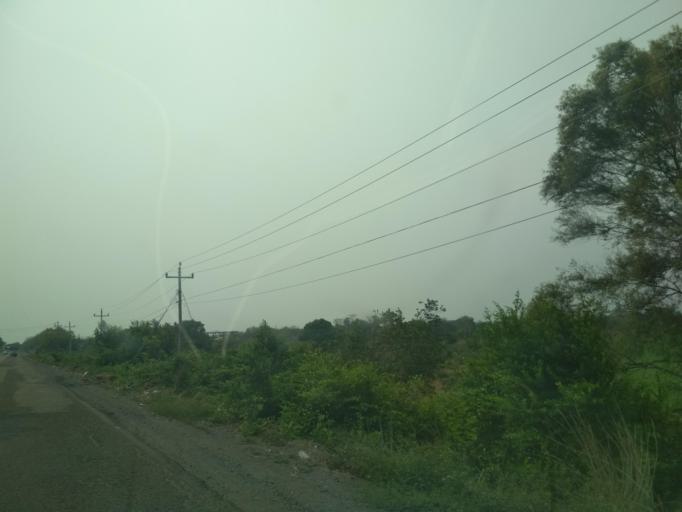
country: MX
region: Veracruz
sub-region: Veracruz
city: Delfino Victoria (Santa Fe)
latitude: 19.2011
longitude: -96.3071
